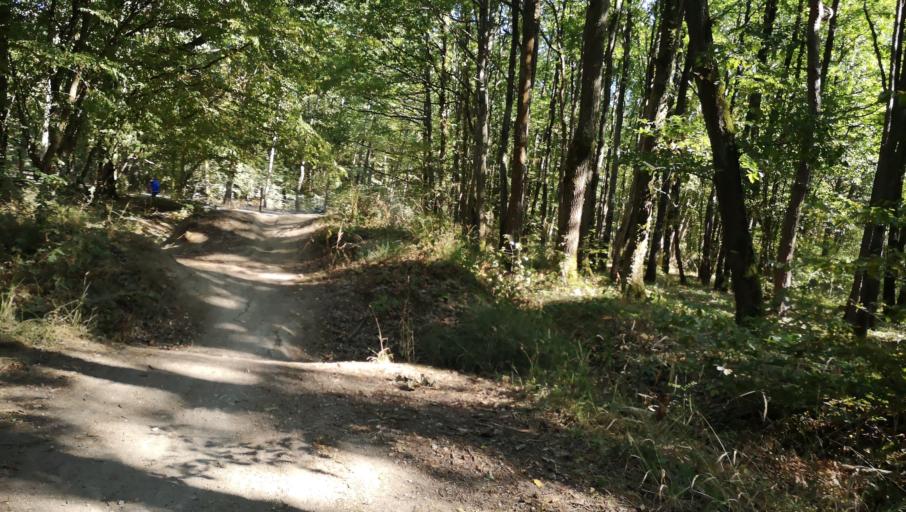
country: FR
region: Centre
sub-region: Departement du Loiret
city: Saran
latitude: 47.9608
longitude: 1.8952
